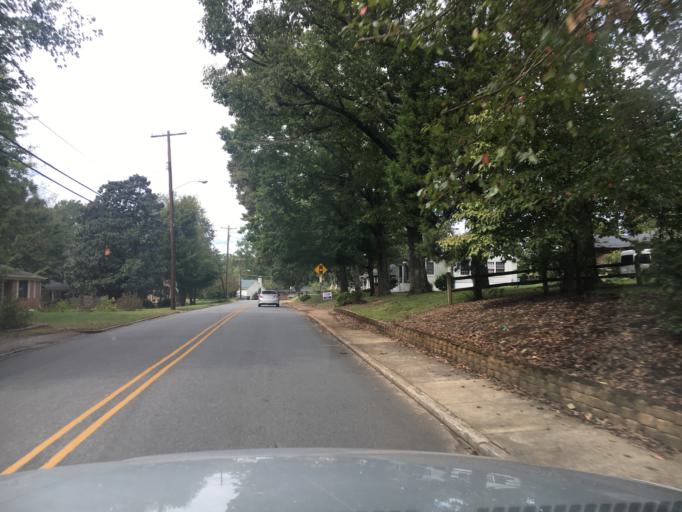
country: US
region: North Carolina
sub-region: Catawba County
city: Hickory
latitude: 35.7430
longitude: -81.3399
